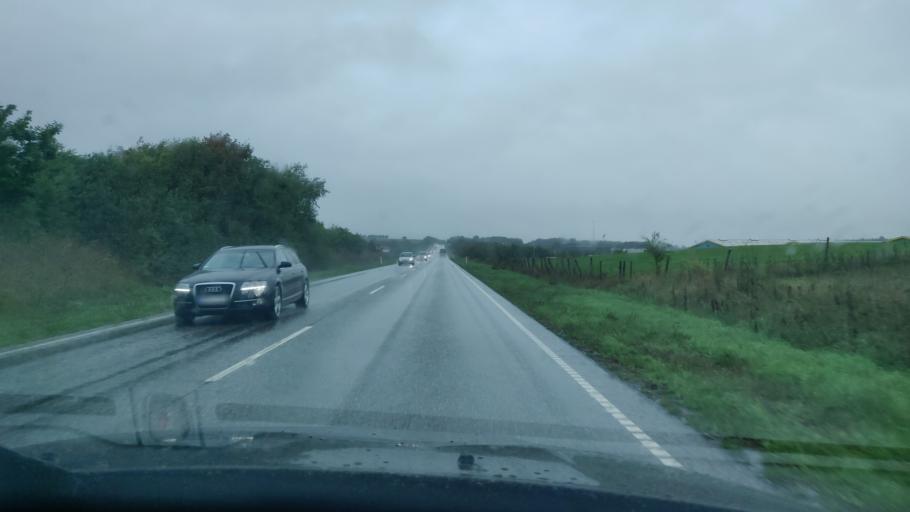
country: DK
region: North Denmark
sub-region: Thisted Kommune
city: Thisted
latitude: 56.9546
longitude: 8.6434
